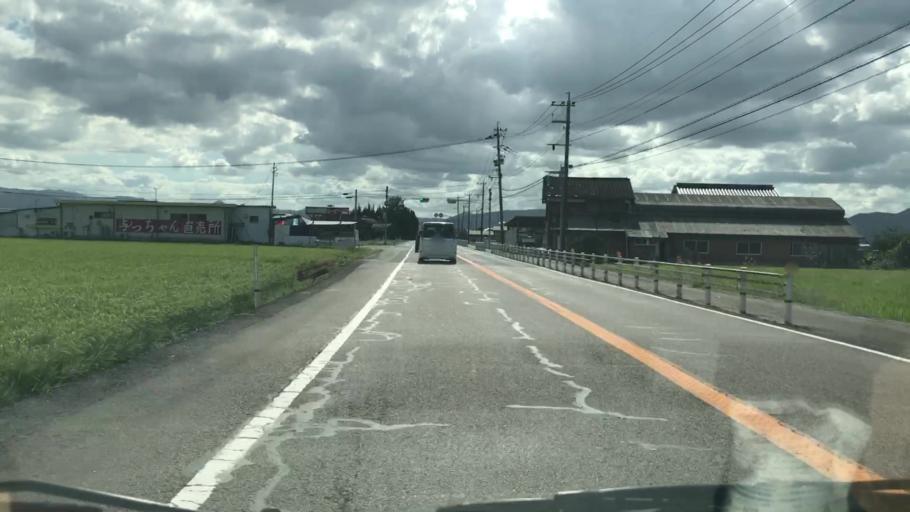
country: JP
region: Saga Prefecture
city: Kashima
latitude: 33.1680
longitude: 130.1768
